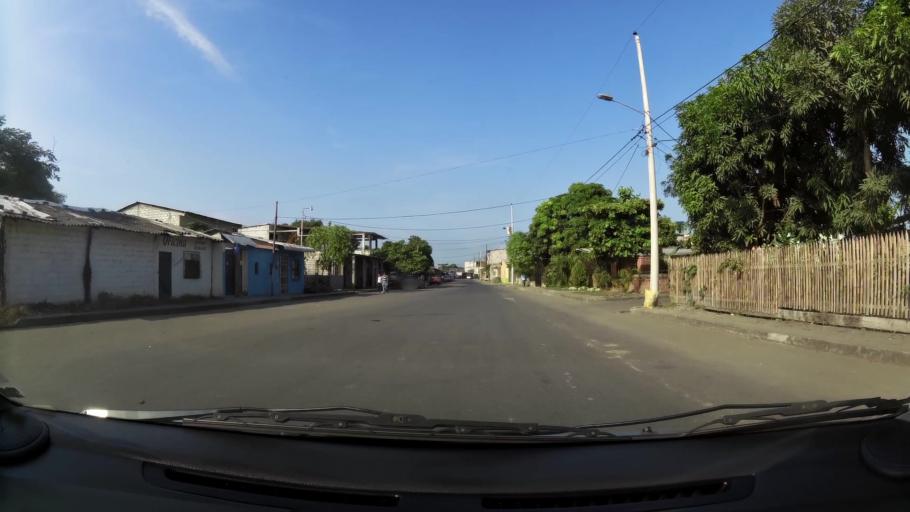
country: EC
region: Guayas
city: Eloy Alfaro
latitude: -2.1838
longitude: -79.8388
